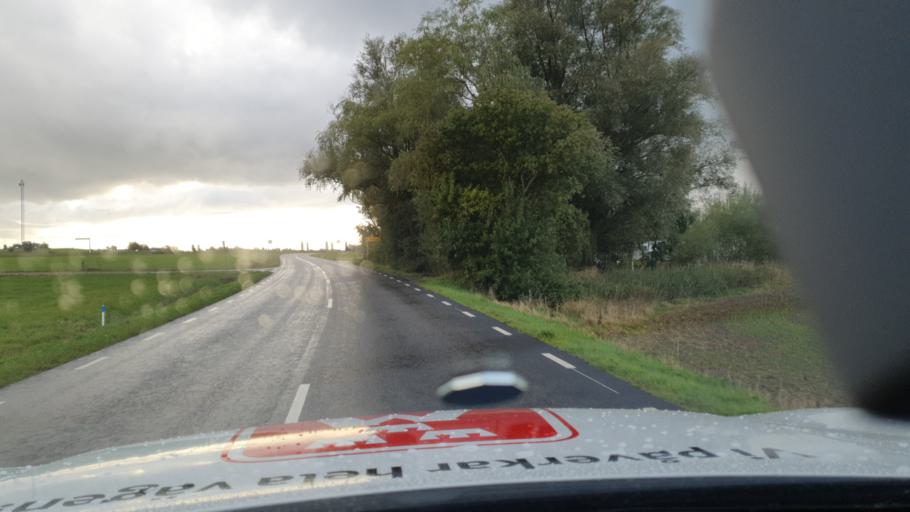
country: SE
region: Skane
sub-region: Trelleborgs Kommun
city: Anderslov
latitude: 55.4226
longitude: 13.2965
